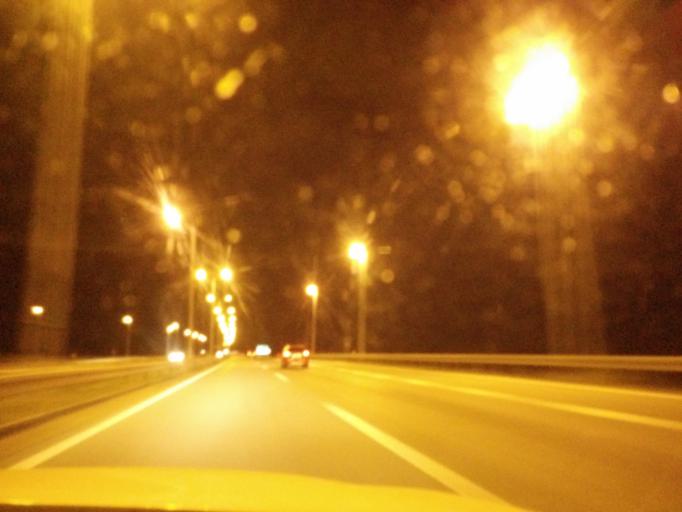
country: RS
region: Autonomna Pokrajina Vojvodina
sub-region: Sremski Okrug
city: Pecinci
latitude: 44.9238
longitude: 19.9511
